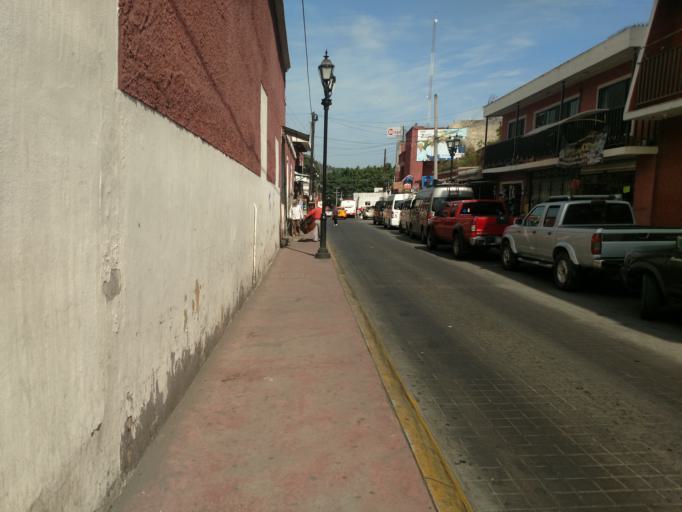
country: MX
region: Nayarit
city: Tepic
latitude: 21.5137
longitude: -104.8901
